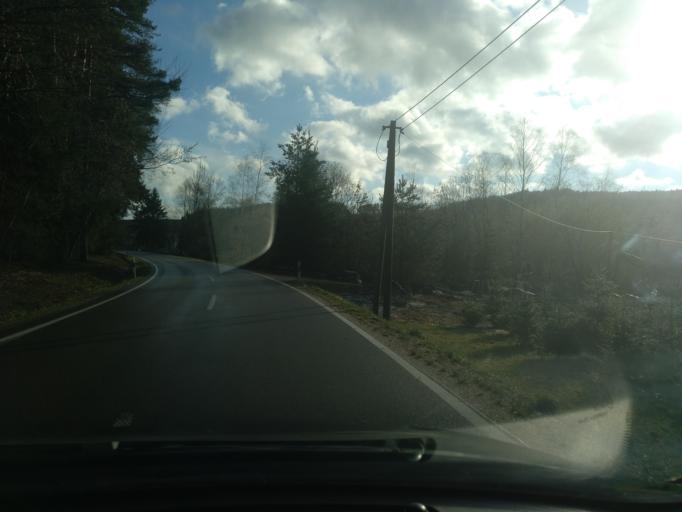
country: DE
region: Bavaria
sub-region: Lower Bavaria
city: Konzell
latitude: 49.1116
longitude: 12.7141
